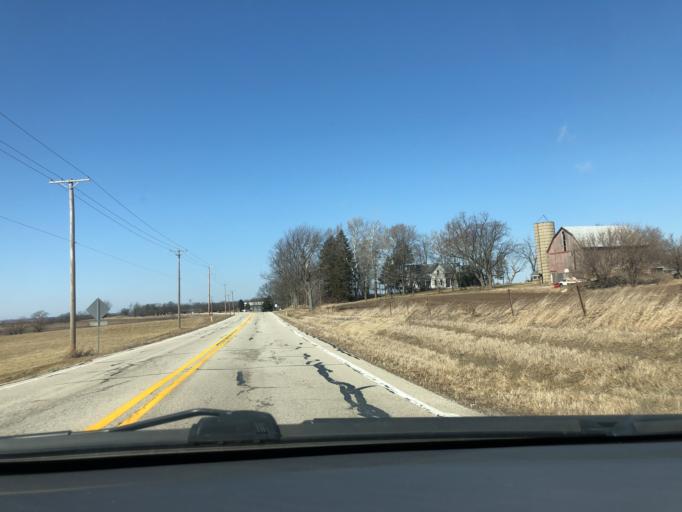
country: US
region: Illinois
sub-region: Kane County
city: Hampshire
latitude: 42.1253
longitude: -88.5120
